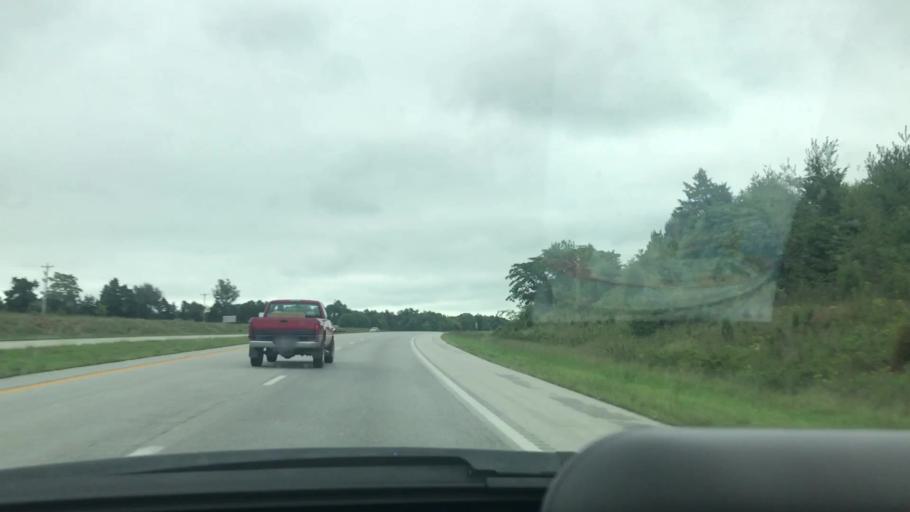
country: US
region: Missouri
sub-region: Greene County
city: Strafford
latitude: 37.2805
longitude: -93.2039
